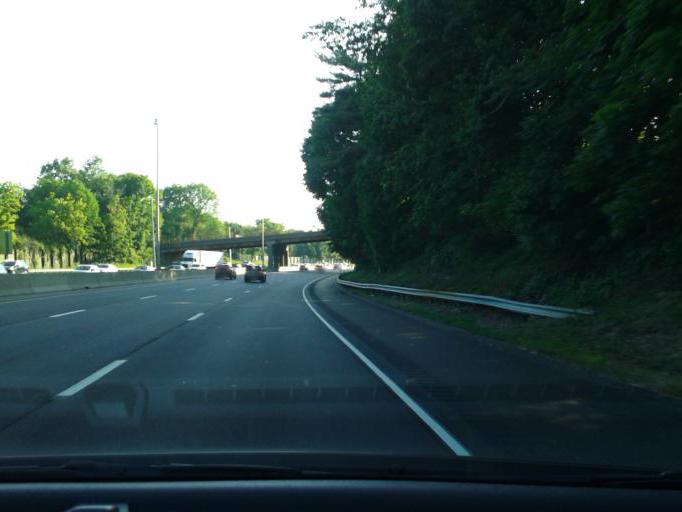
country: US
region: Connecticut
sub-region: Fairfield County
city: Darien
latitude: 41.0691
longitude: -73.4891
